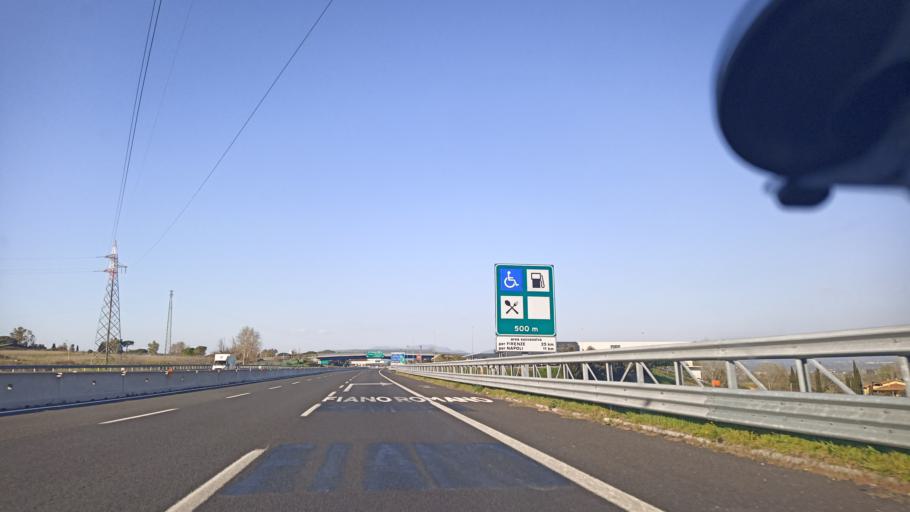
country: IT
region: Latium
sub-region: Citta metropolitana di Roma Capitale
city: Bivio di Capanelle
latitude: 42.1256
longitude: 12.5971
